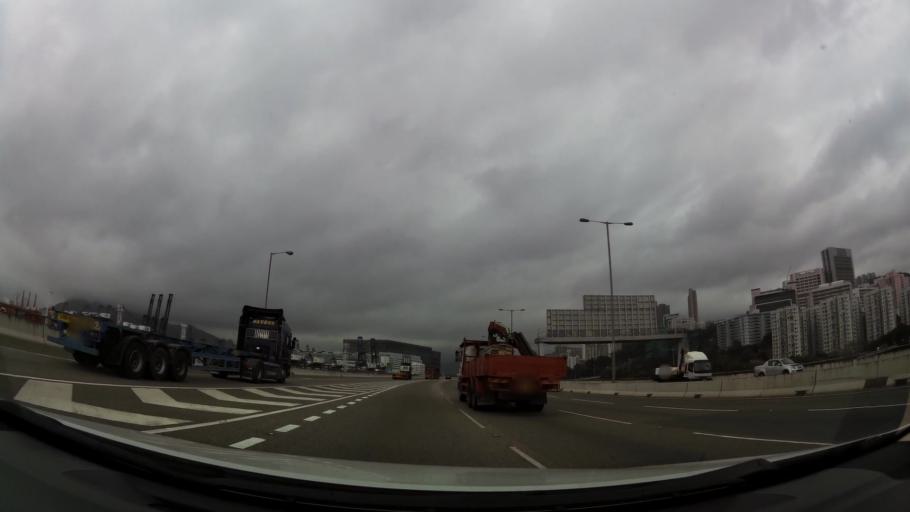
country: HK
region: Sham Shui Po
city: Sham Shui Po
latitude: 22.3357
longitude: 114.1339
